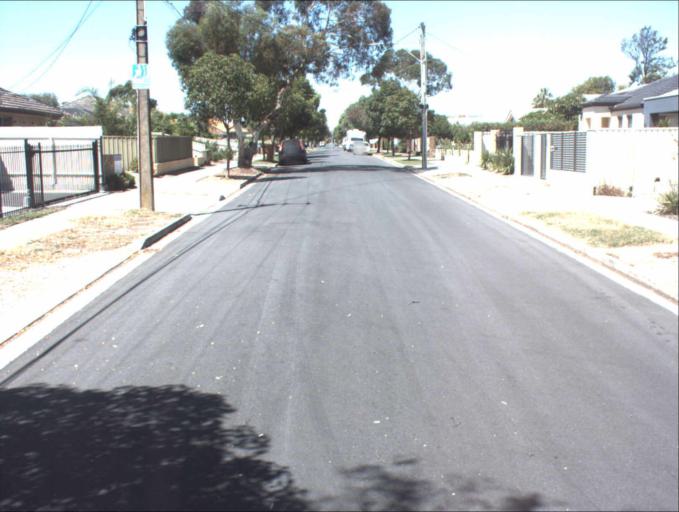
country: AU
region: South Australia
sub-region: Port Adelaide Enfield
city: Blair Athol
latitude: -34.8685
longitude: 138.6071
